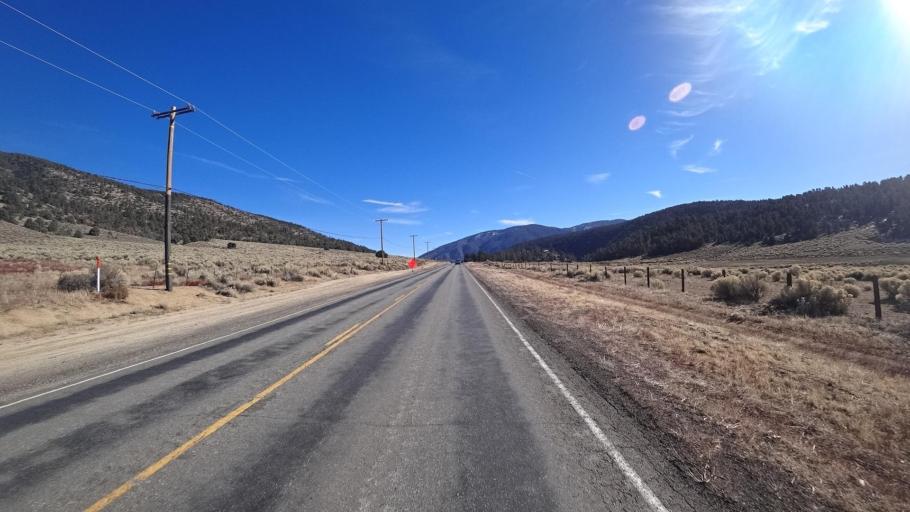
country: US
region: California
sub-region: Kern County
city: Frazier Park
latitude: 34.8332
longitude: -119.0318
